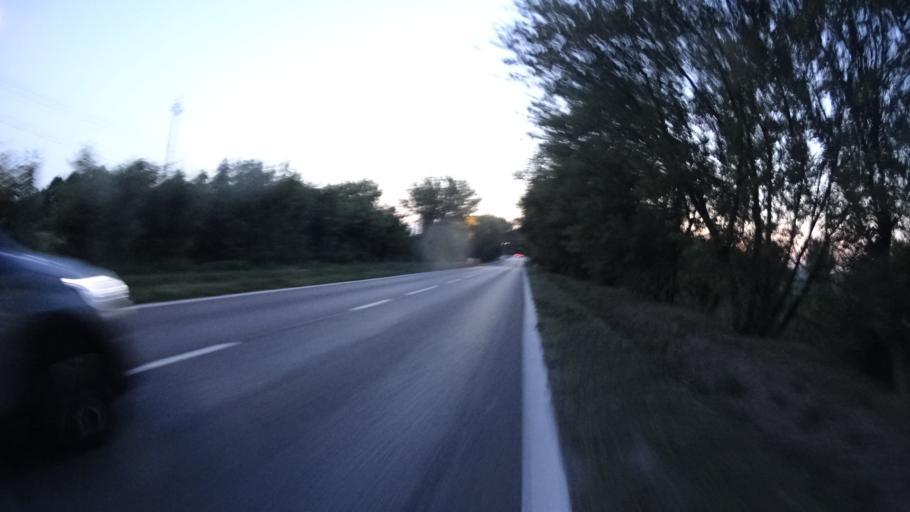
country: PL
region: Masovian Voivodeship
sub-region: Powiat warszawski zachodni
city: Jozefow
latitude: 52.2630
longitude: 20.6700
